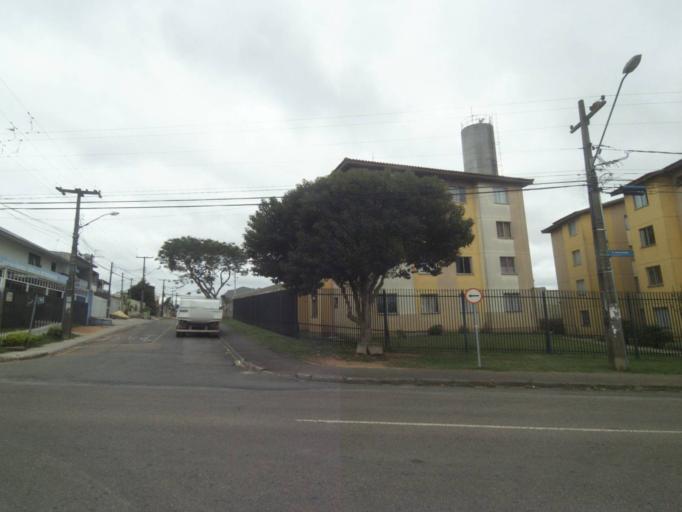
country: BR
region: Parana
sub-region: Sao Jose Dos Pinhais
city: Sao Jose dos Pinhais
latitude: -25.5466
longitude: -49.2667
